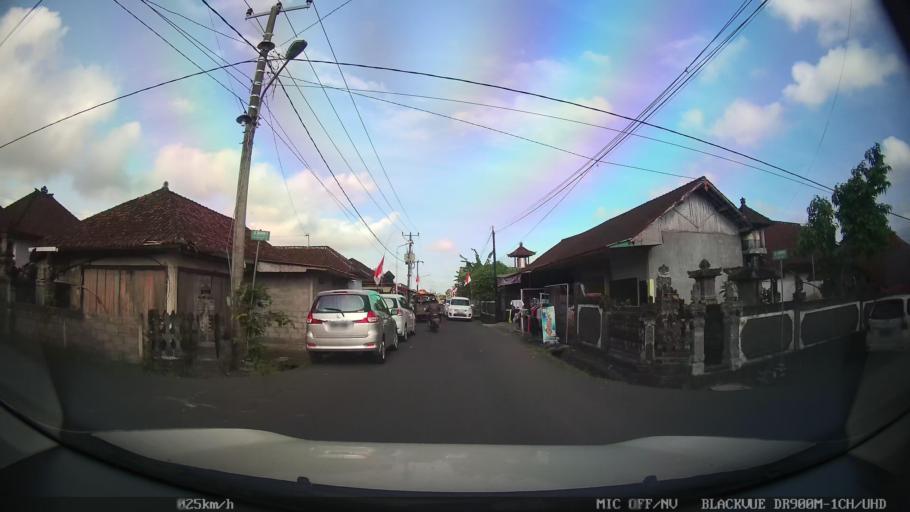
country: ID
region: Bali
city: Banjar Pekenjelodan
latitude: -8.5693
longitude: 115.1828
